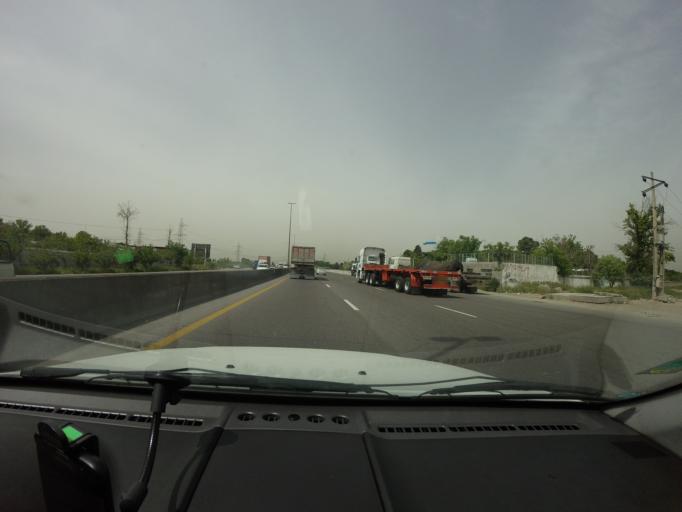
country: IR
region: Tehran
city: Eslamshahr
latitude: 35.6215
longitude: 51.2267
